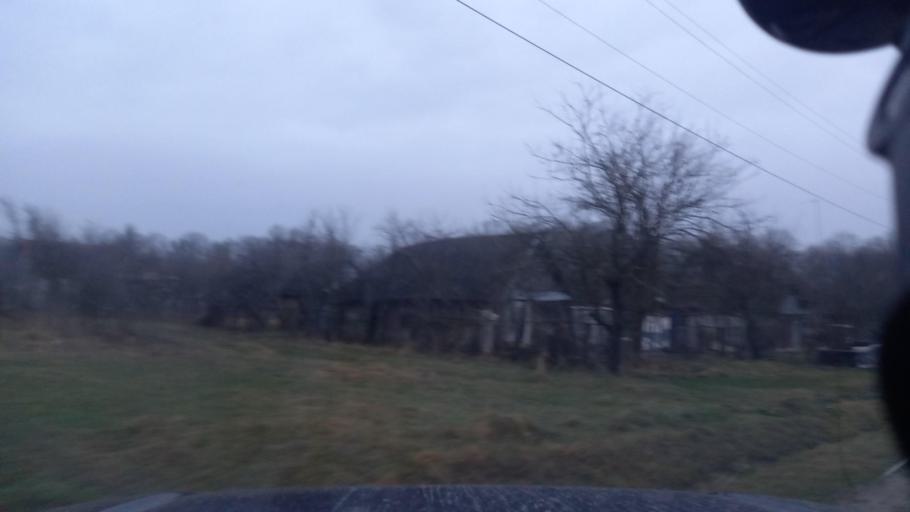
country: RU
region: Krasnodarskiy
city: Saratovskaya
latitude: 44.6475
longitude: 39.3197
